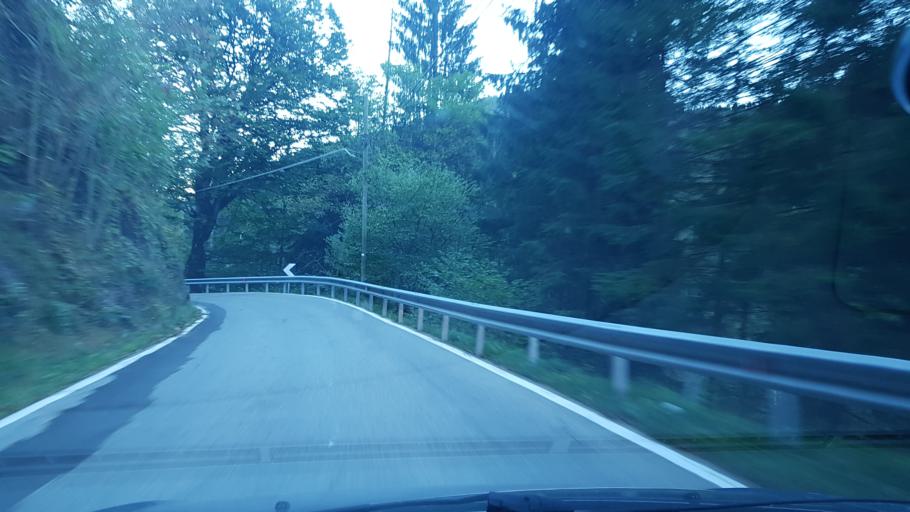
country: IT
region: Veneto
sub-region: Provincia di Belluno
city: Fusine
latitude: 46.3479
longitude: 12.1316
